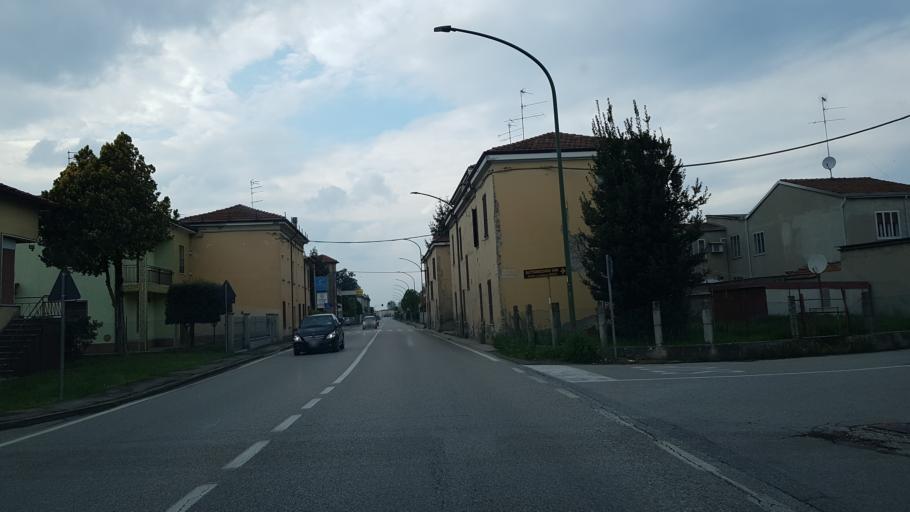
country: IT
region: Lombardy
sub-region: Provincia di Mantova
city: Ostiglia
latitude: 45.0674
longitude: 11.1411
